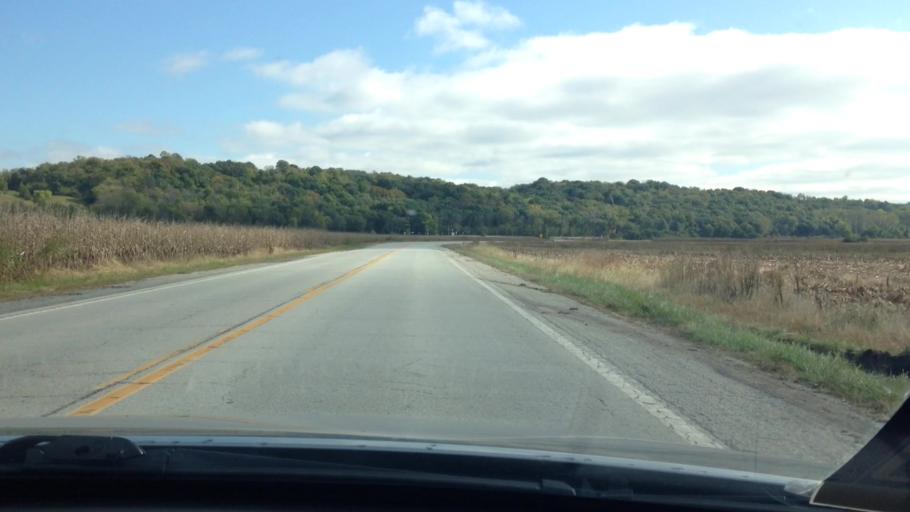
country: US
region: Kansas
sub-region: Leavenworth County
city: Leavenworth
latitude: 39.3239
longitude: -94.8628
